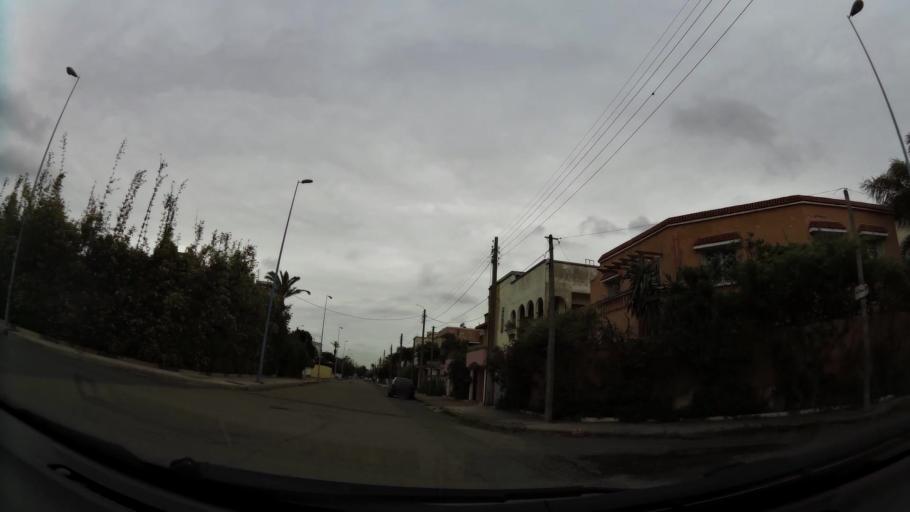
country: MA
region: Grand Casablanca
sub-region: Casablanca
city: Casablanca
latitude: 33.5644
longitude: -7.6237
